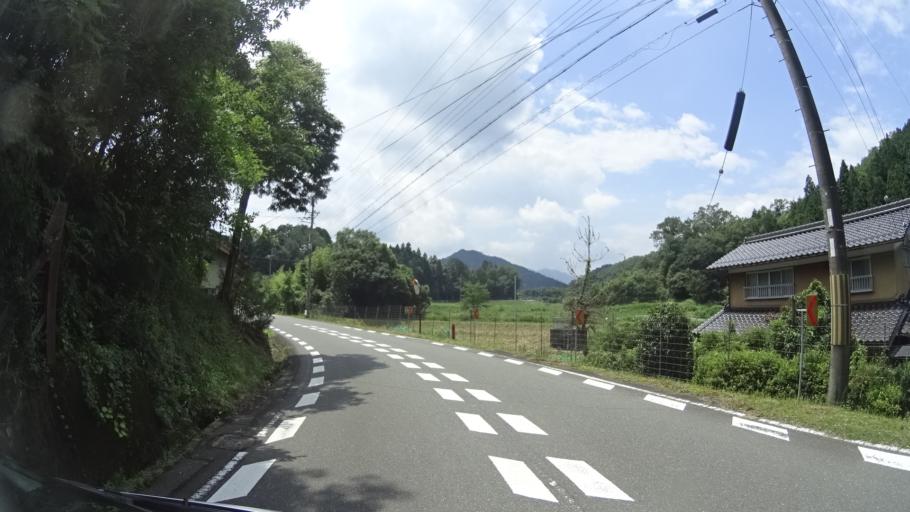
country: JP
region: Hyogo
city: Sasayama
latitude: 35.1755
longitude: 135.2779
